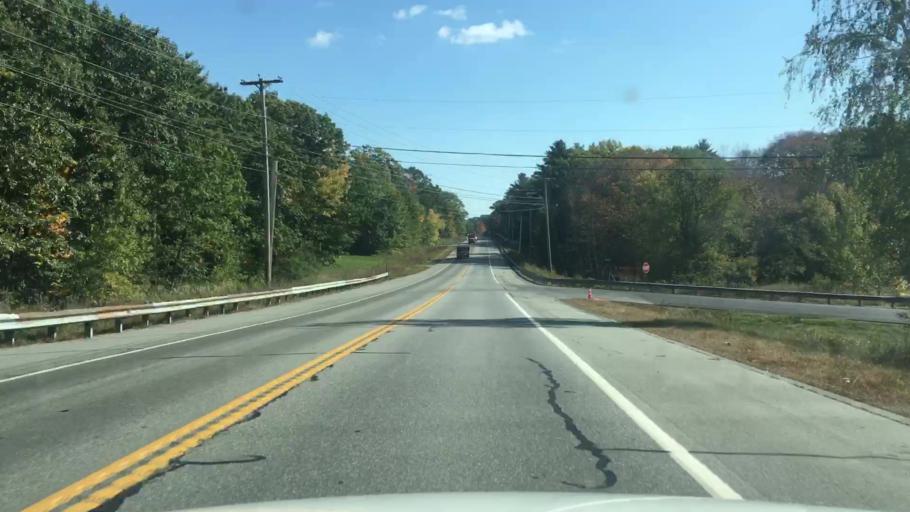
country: US
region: Maine
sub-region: Knox County
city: Warren
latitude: 44.1195
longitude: -69.2741
